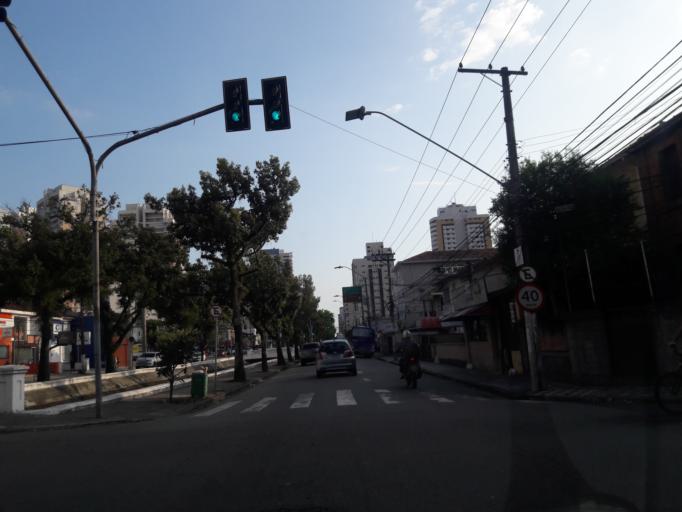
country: BR
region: Sao Paulo
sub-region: Santos
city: Santos
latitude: -23.9602
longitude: -46.3383
